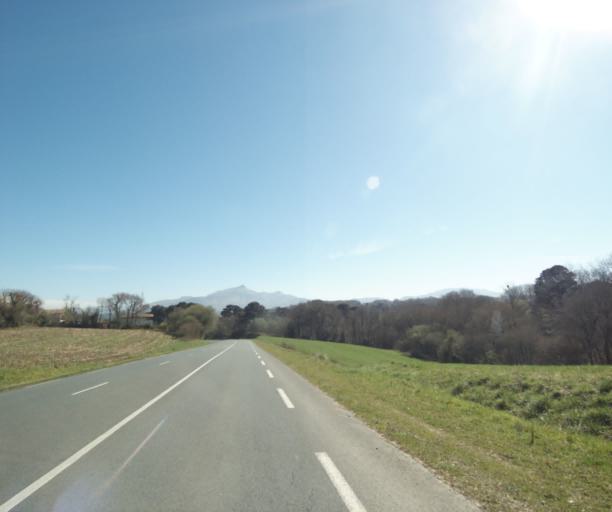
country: FR
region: Aquitaine
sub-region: Departement des Pyrenees-Atlantiques
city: Urrugne
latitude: 43.3863
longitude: -1.6994
